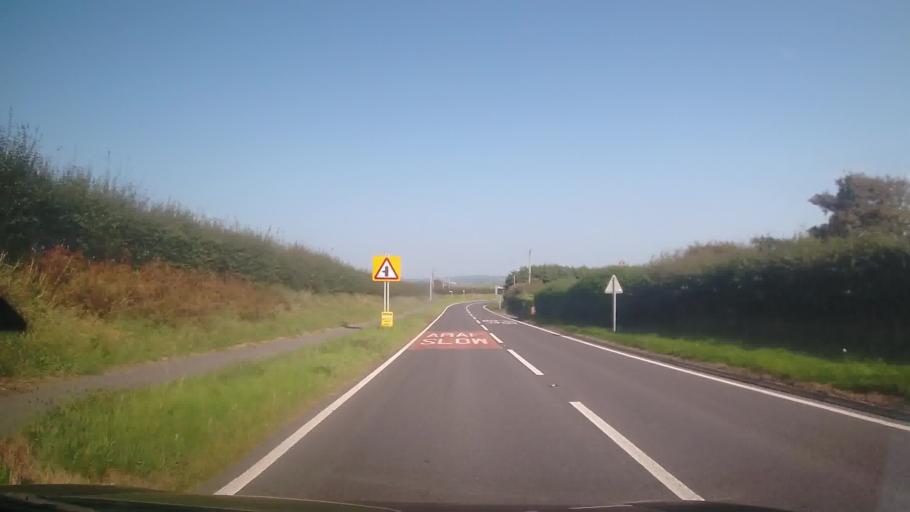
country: GB
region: Wales
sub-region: County of Ceredigion
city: Aberporth
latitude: 52.1060
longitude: -4.5933
